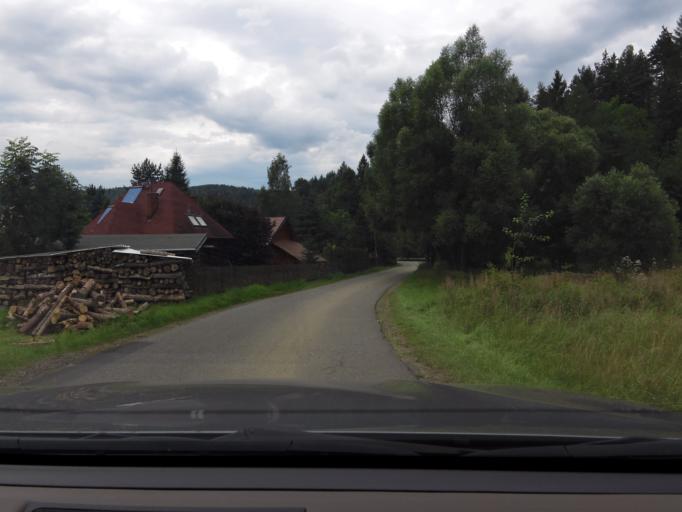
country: PL
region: Silesian Voivodeship
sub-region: Powiat zywiecki
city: Rajcza
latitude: 49.5038
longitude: 19.1166
